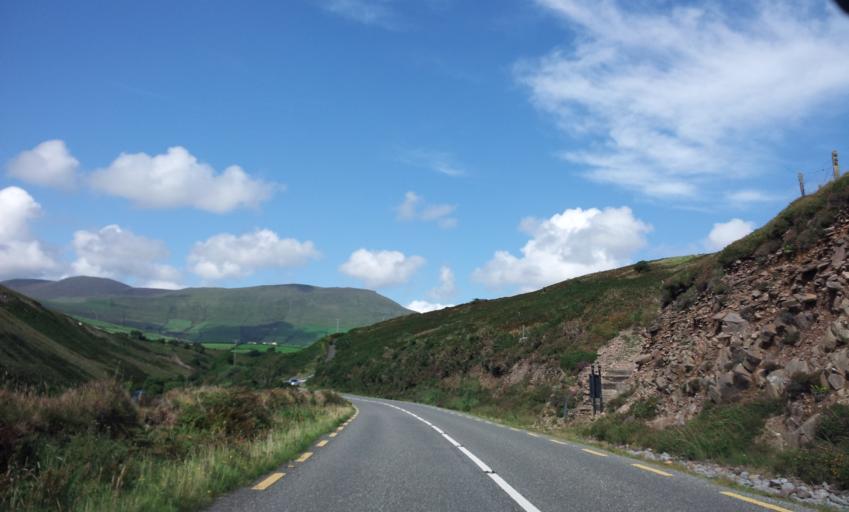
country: IE
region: Munster
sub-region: Ciarrai
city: Dingle
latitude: 52.1387
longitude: -10.0507
